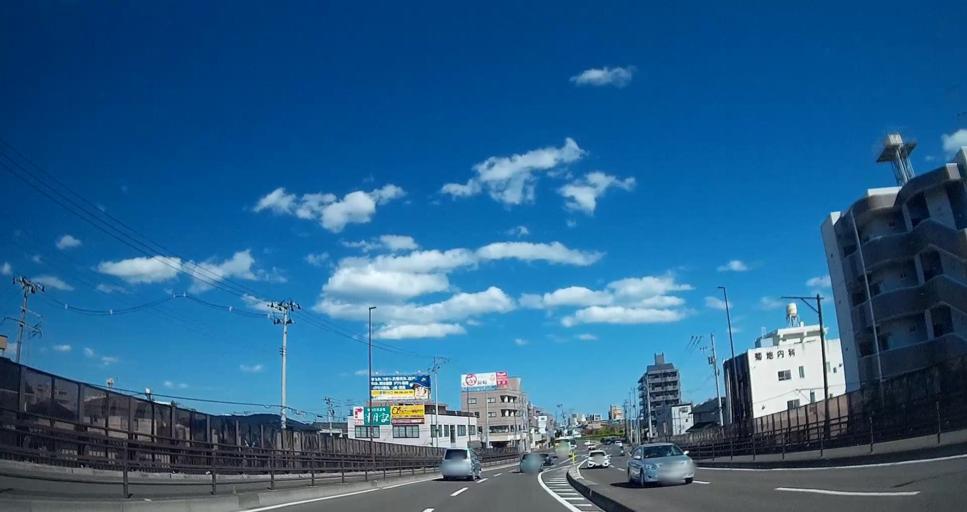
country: JP
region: Miyagi
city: Sendai-shi
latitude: 38.2530
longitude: 140.9071
